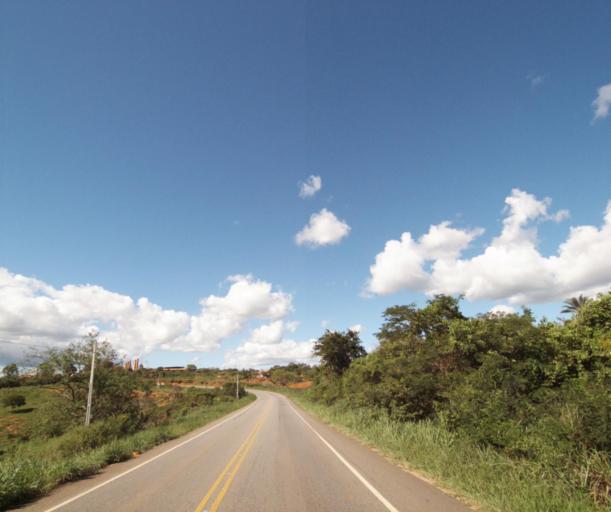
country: BR
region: Bahia
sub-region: Caetite
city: Caetite
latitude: -14.0918
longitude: -42.4476
